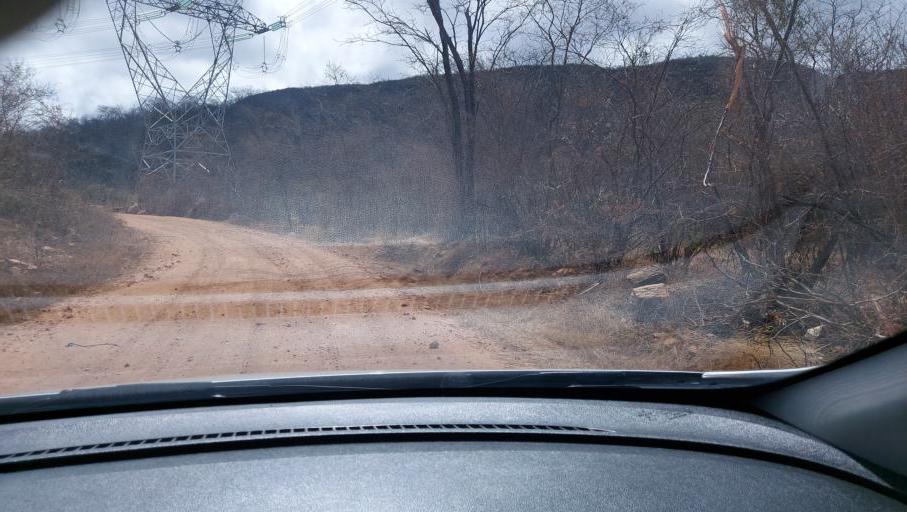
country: BR
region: Bahia
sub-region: Oliveira Dos Brejinhos
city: Beira Rio
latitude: -12.0961
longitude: -42.5440
